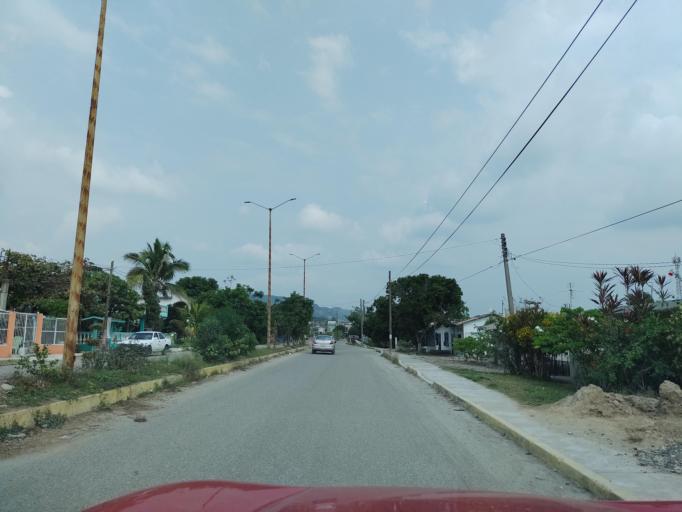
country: MX
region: Veracruz
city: Agua Dulce
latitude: 20.3653
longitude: -97.2942
